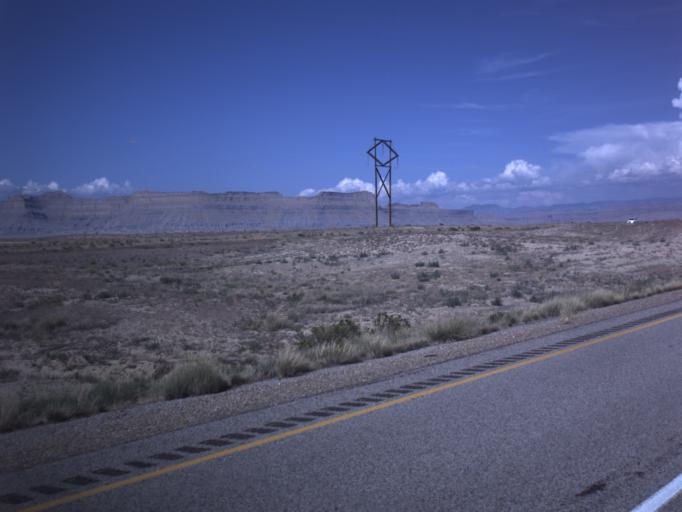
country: US
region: Utah
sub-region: Carbon County
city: East Carbon City
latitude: 38.9656
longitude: -110.2756
